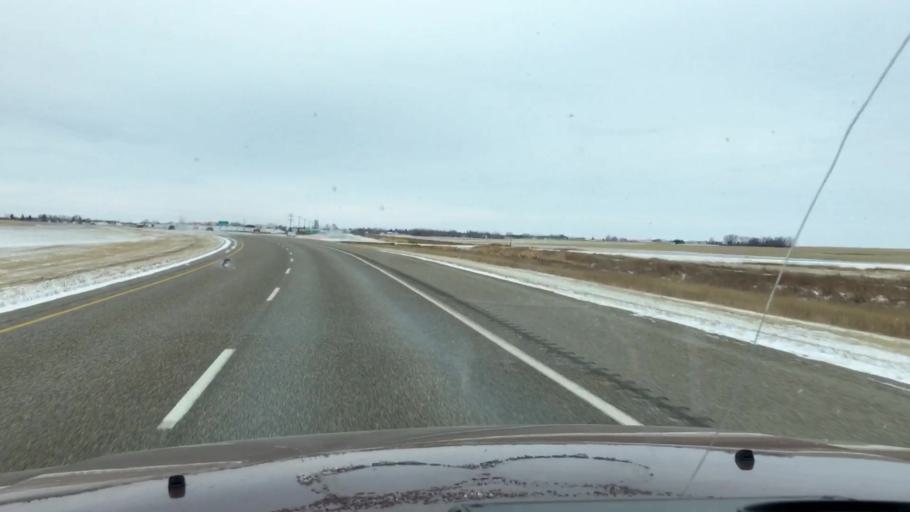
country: CA
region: Saskatchewan
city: Watrous
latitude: 51.0683
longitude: -105.8377
